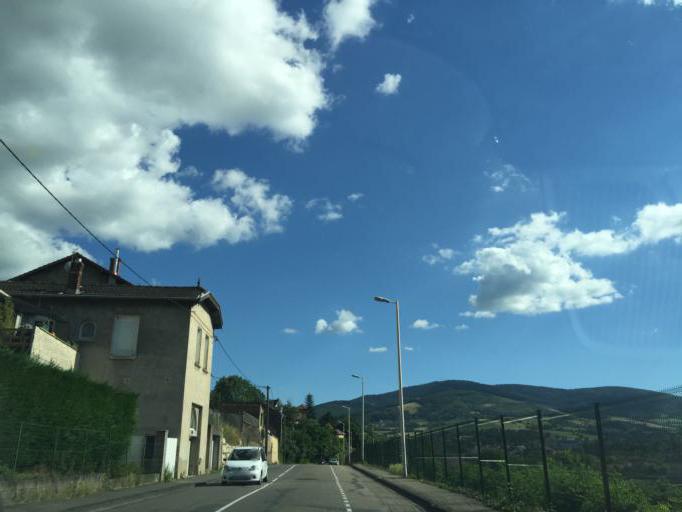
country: FR
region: Rhone-Alpes
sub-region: Departement de la Loire
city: Saint-Chamond
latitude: 45.4679
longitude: 4.5109
